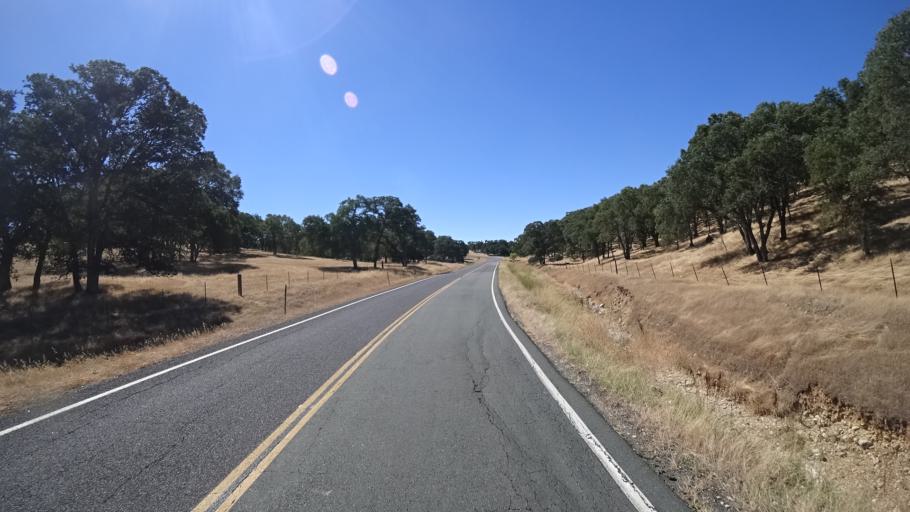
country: US
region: California
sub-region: Calaveras County
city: Rancho Calaveras
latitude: 38.0752
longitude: -120.8705
